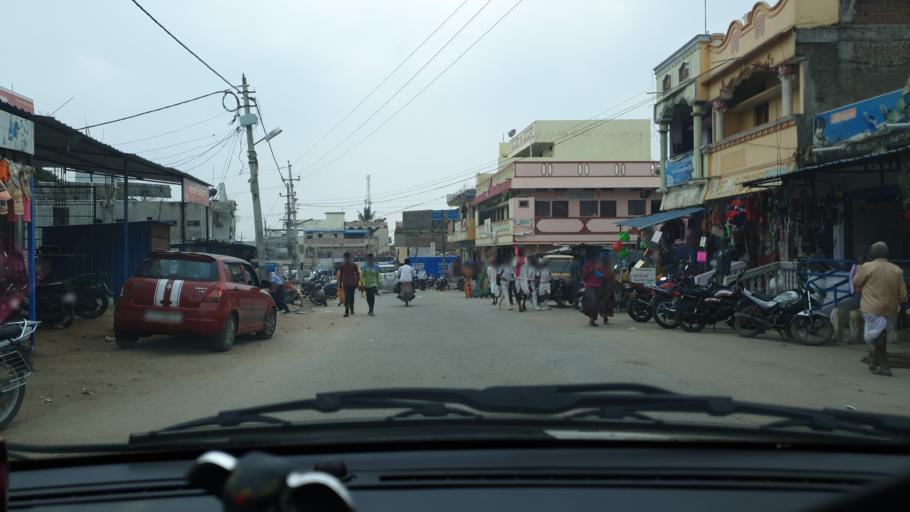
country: IN
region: Karnataka
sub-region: Yadgir
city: Gurmatkal
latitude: 16.8699
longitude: 77.3911
